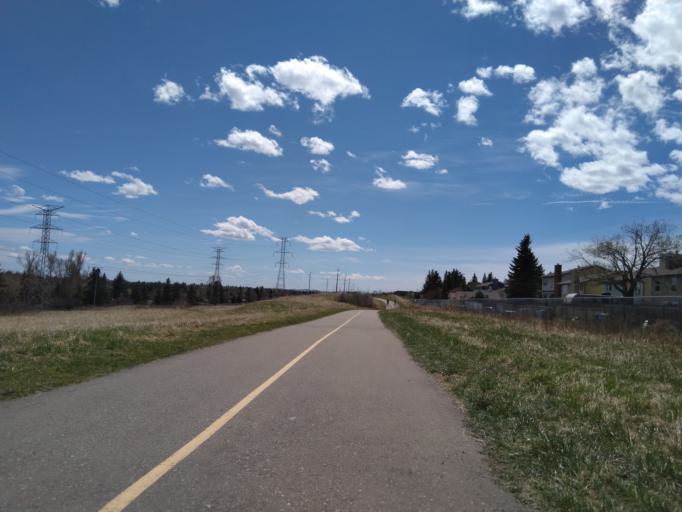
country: CA
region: Alberta
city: Calgary
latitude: 51.0471
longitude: -114.1653
